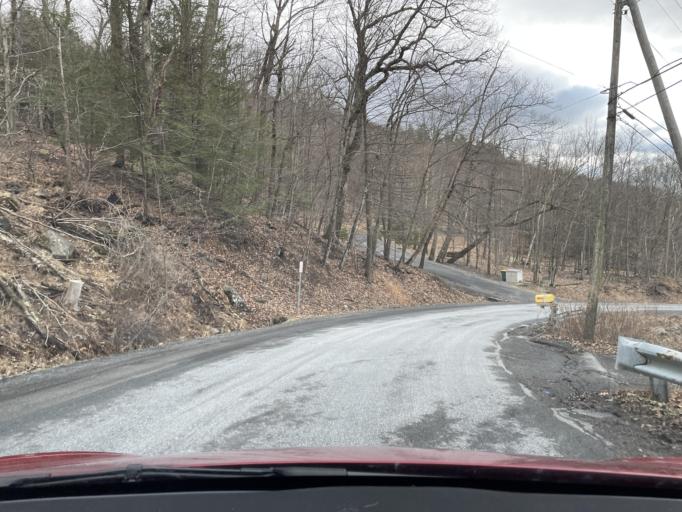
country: US
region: New York
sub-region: Ulster County
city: Woodstock
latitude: 42.0689
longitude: -74.1225
